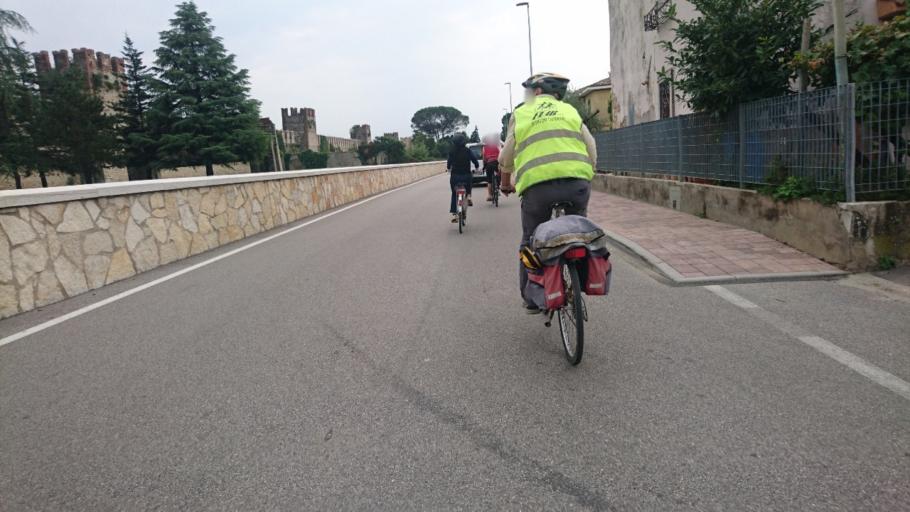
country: IT
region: Veneto
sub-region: Provincia di Verona
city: Soave
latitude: 45.4234
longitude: 11.2455
